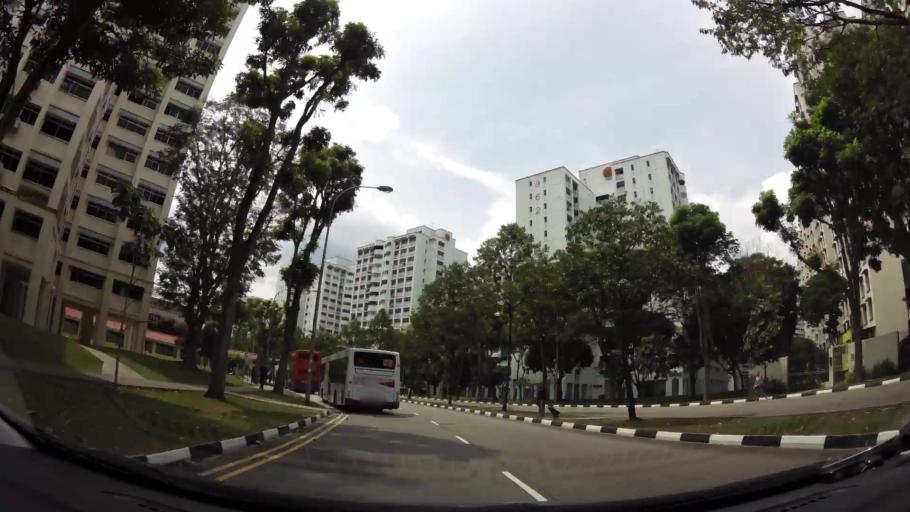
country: MY
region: Johor
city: Johor Bahru
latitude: 1.3502
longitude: 103.6977
